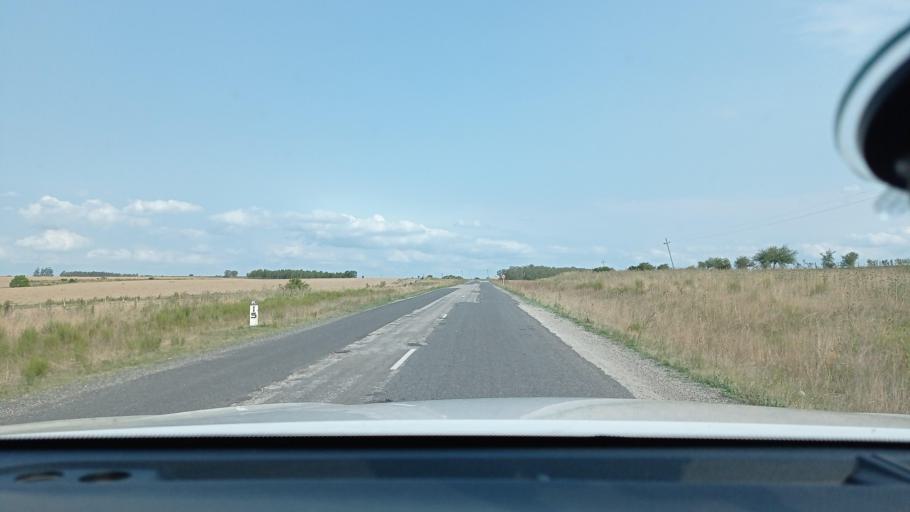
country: UY
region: Canelones
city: San Ramon
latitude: -34.2007
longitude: -56.0441
